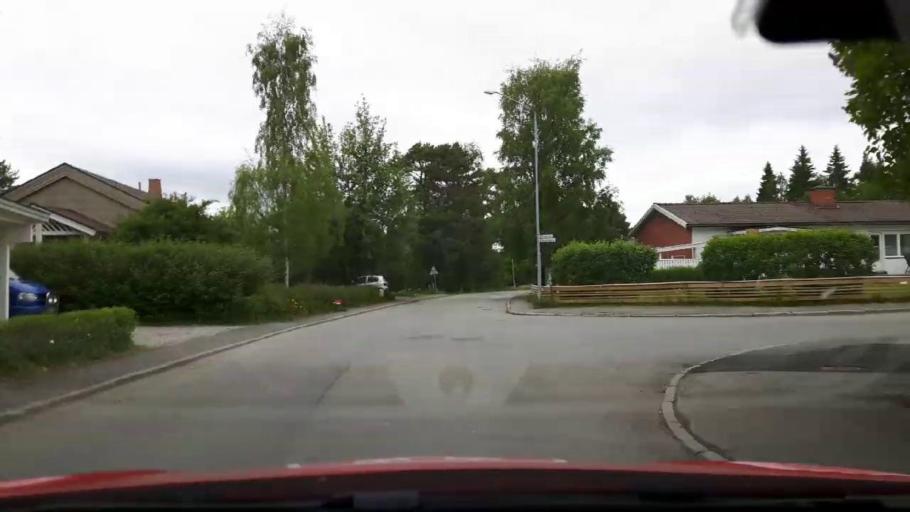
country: SE
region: Jaemtland
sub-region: OEstersunds Kommun
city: Ostersund
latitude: 63.2081
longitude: 14.6209
